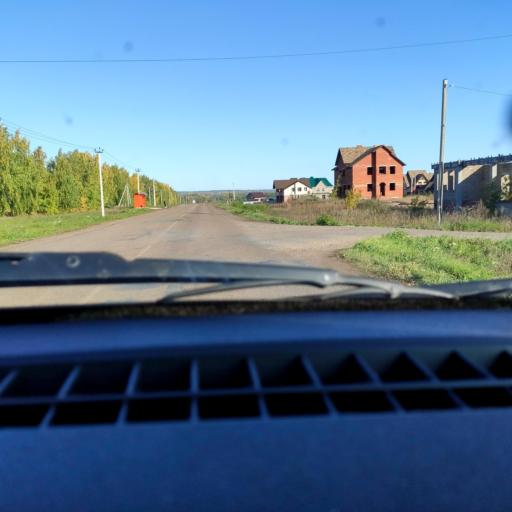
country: RU
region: Bashkortostan
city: Avdon
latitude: 54.5945
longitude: 55.8002
